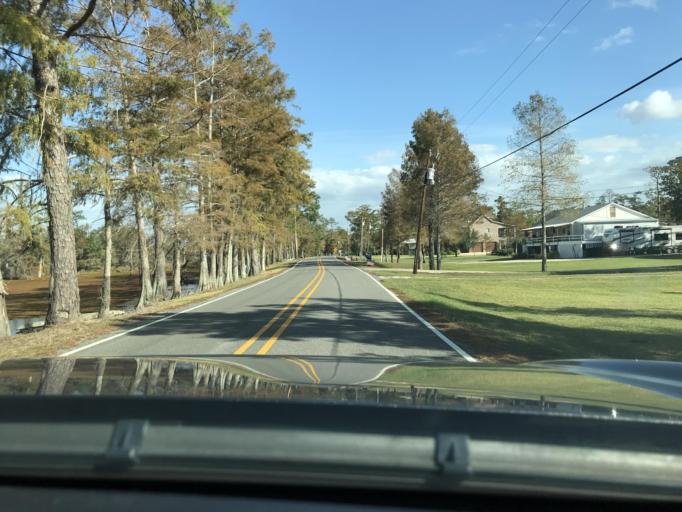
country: US
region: Louisiana
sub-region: Calcasieu Parish
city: Westlake
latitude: 30.3163
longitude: -93.2907
